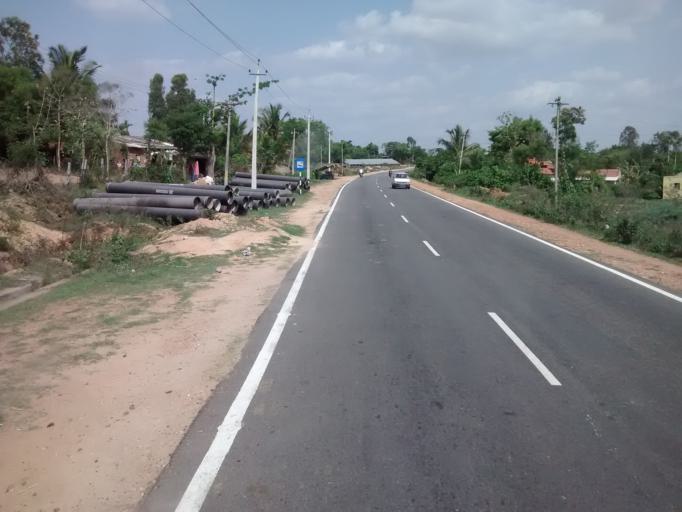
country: IN
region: Karnataka
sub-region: Mysore
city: Hunsur
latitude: 12.3627
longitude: 76.4211
